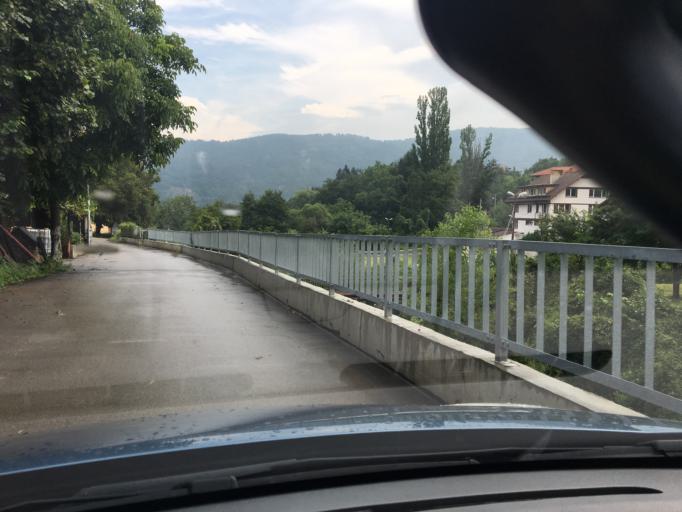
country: BG
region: Sofia-Capital
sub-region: Stolichna Obshtina
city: Sofia
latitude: 42.5900
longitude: 23.4085
